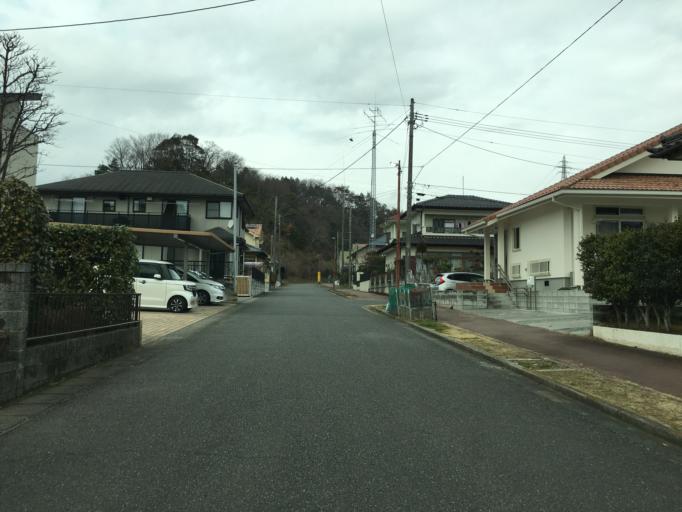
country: JP
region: Fukushima
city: Iwaki
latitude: 36.9651
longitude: 140.8529
